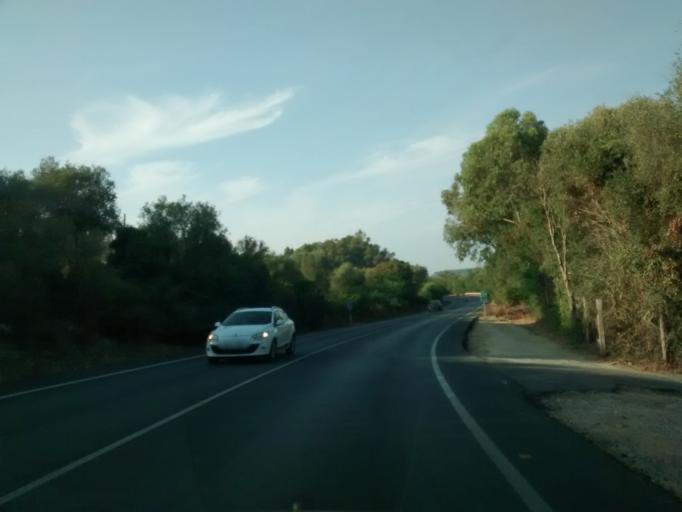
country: ES
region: Andalusia
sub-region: Provincia de Cadiz
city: Vejer de la Frontera
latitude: 36.2275
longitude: -5.9488
